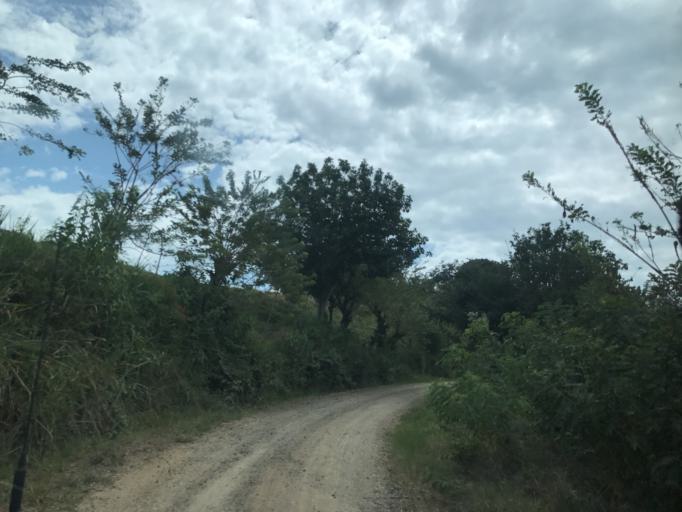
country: CO
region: Valle del Cauca
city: Obando
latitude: 4.5642
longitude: -75.9392
